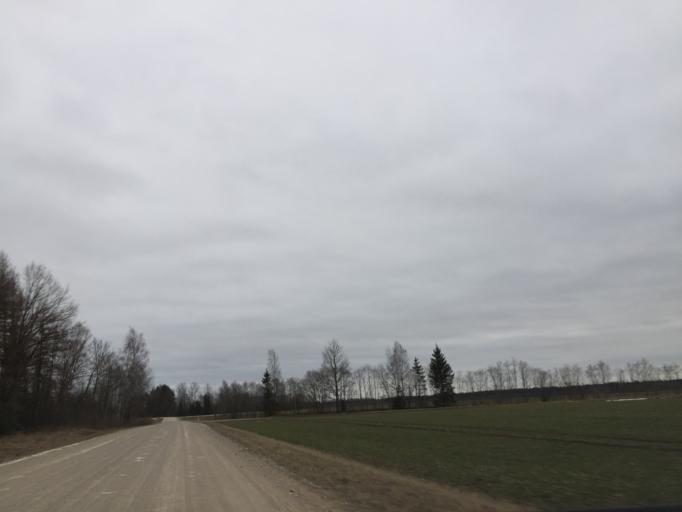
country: LT
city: Zagare
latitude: 56.2892
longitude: 23.2600
